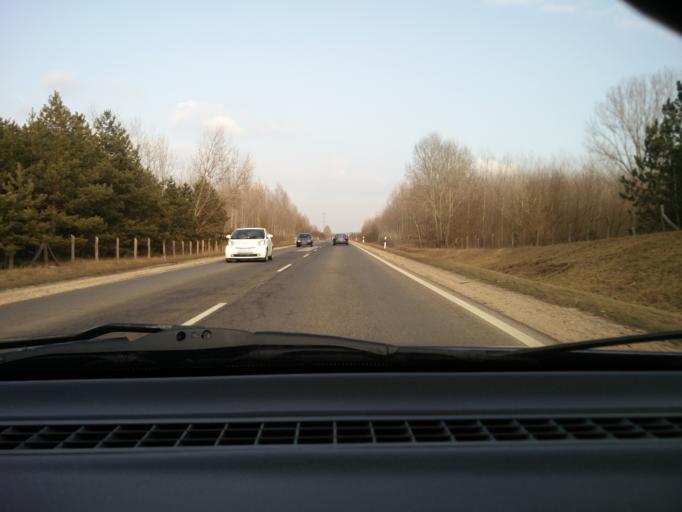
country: HU
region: Pest
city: Ujhartyan
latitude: 47.2365
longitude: 19.4274
